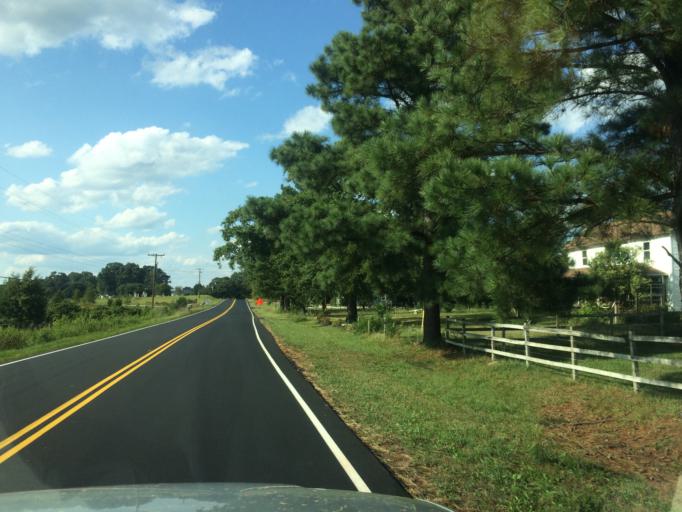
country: US
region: South Carolina
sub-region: Greenwood County
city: Ware Shoals
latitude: 34.4902
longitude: -82.1787
